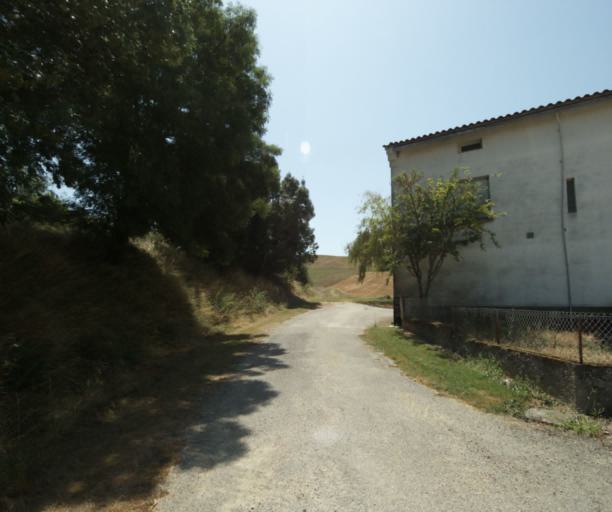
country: FR
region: Midi-Pyrenees
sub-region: Departement de la Haute-Garonne
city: Saint-Felix-Lauragais
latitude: 43.4448
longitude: 1.8813
